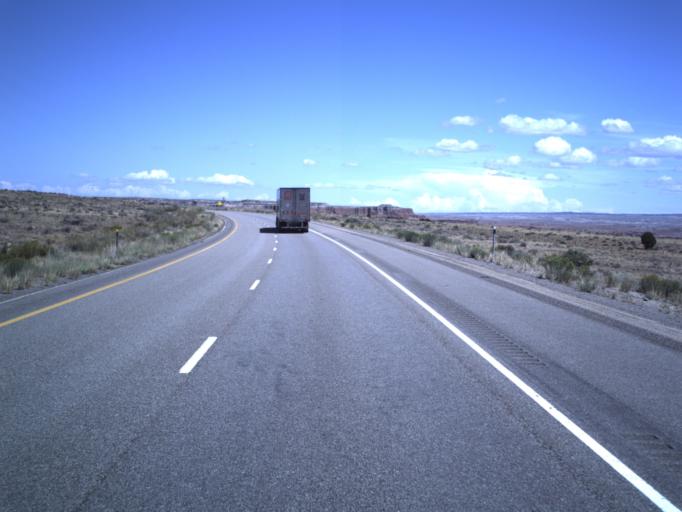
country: US
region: Utah
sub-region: Emery County
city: Ferron
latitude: 38.8323
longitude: -111.1064
